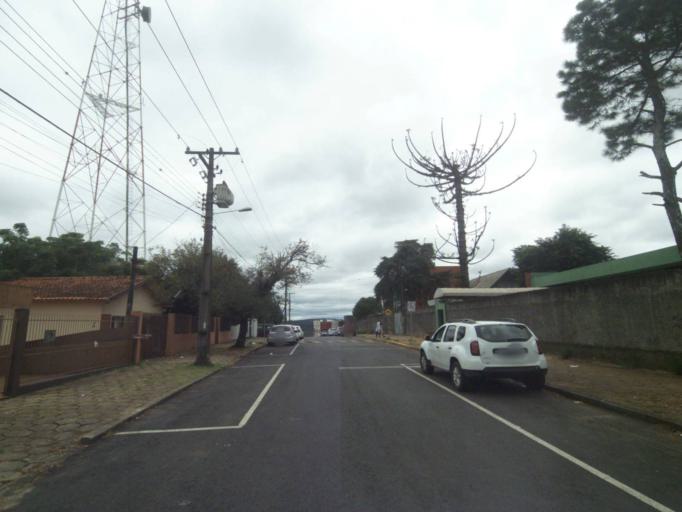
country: BR
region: Parana
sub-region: Telemaco Borba
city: Telemaco Borba
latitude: -24.3287
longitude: -50.6173
